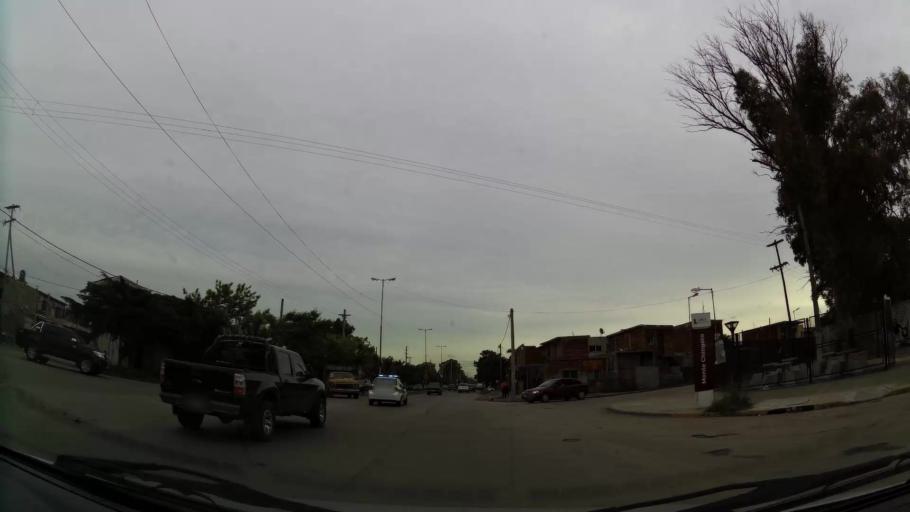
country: AR
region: Buenos Aires
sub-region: Partido de Lanus
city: Lanus
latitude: -34.7200
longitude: -58.3496
